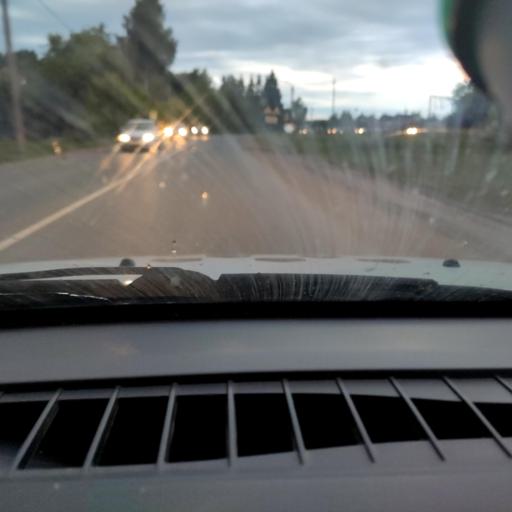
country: RU
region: Udmurtiya
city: Glazov
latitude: 58.1252
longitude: 52.6994
